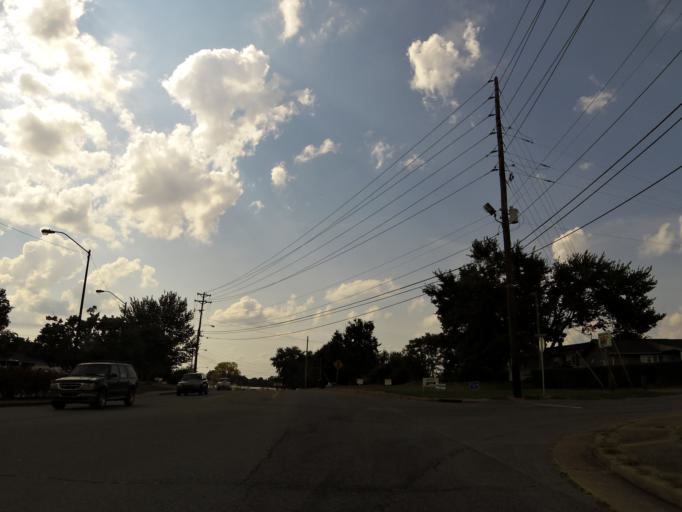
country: US
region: Tennessee
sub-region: Dickson County
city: Dickson
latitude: 36.0696
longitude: -87.3829
